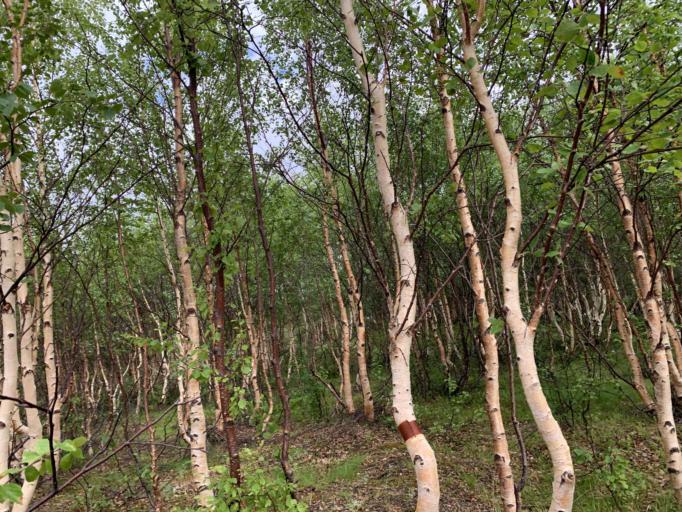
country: RU
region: Murmansk
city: Monchegorsk
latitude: 67.7969
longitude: 32.8124
